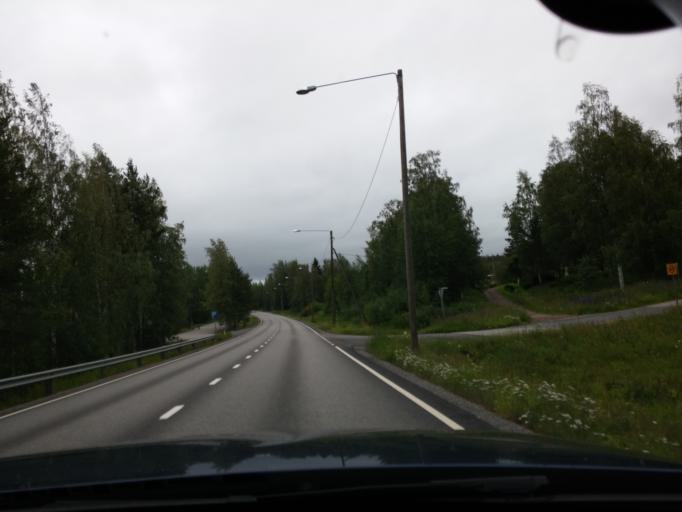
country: FI
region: Central Finland
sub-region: Saarijaervi-Viitasaari
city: Saarijaervi
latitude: 62.6917
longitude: 25.2759
